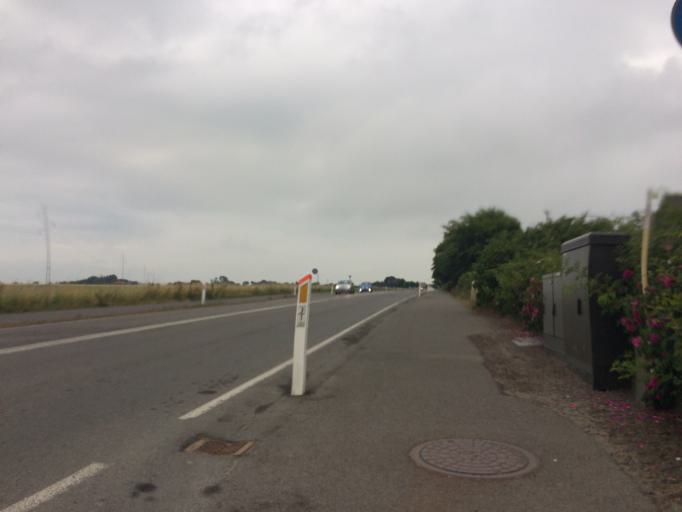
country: DK
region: Capital Region
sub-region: Bornholm Kommune
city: Ronne
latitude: 55.1066
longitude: 14.7392
